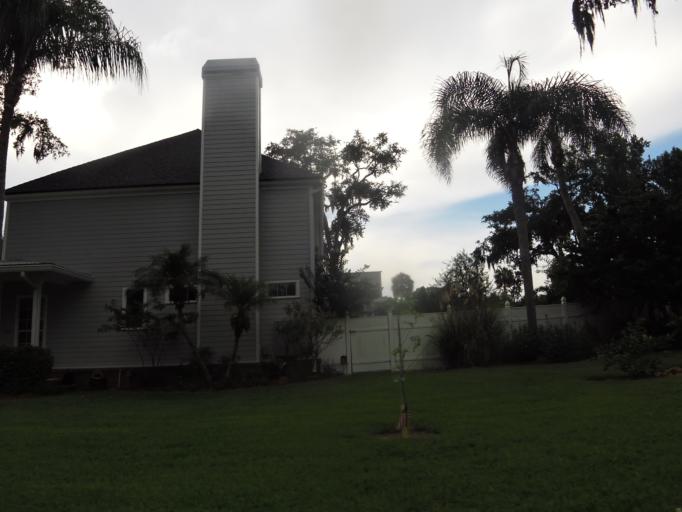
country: US
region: Florida
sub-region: Duval County
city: Jacksonville Beach
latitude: 30.2709
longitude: -81.4064
